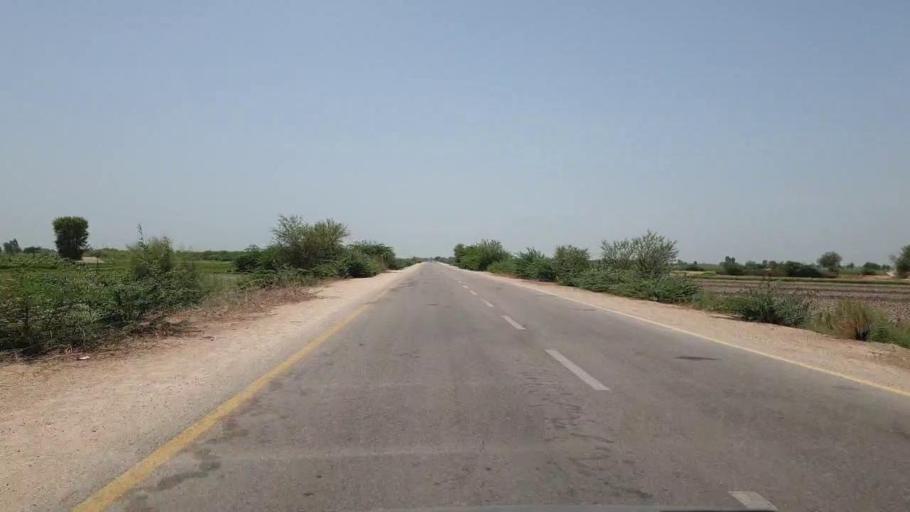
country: PK
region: Sindh
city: Sakrand
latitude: 26.1371
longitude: 68.3724
